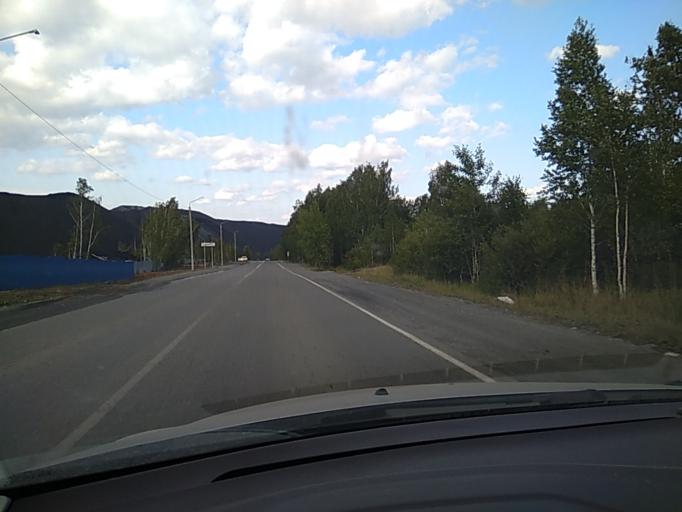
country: RU
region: Chelyabinsk
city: Karabash
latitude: 55.4925
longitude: 60.2441
